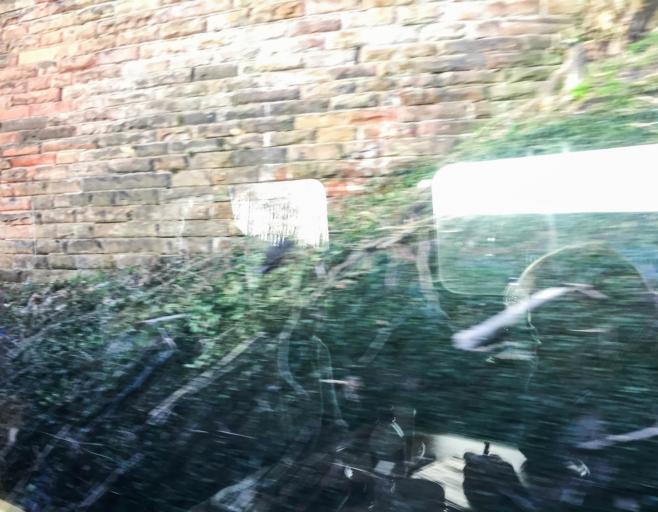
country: GB
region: England
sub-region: Cumbria
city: Carlisle
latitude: 54.8949
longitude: -2.9425
